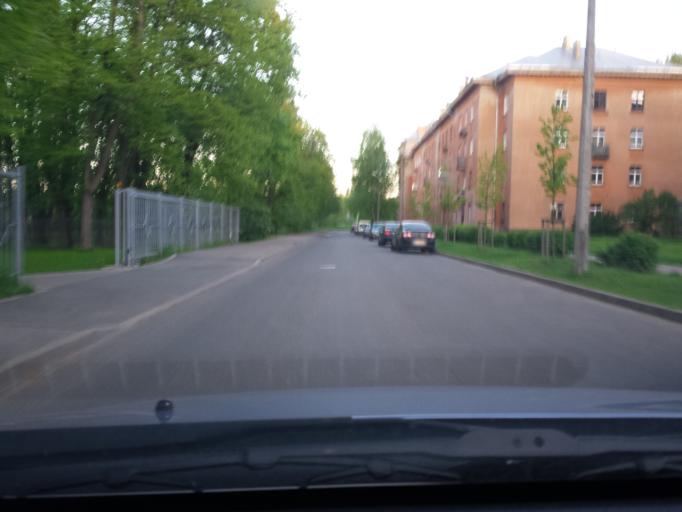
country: LV
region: Riga
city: Riga
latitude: 56.9887
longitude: 24.1367
